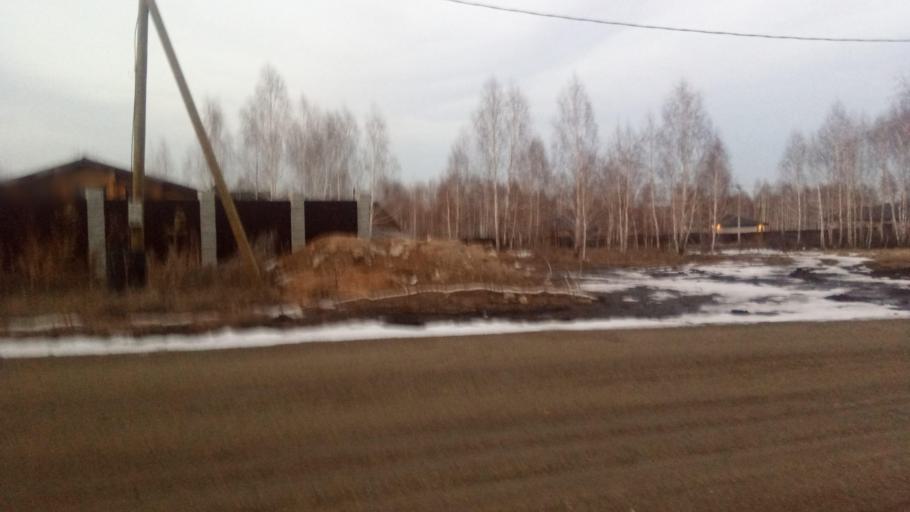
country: RU
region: Chelyabinsk
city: Sargazy
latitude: 55.1025
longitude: 61.2028
